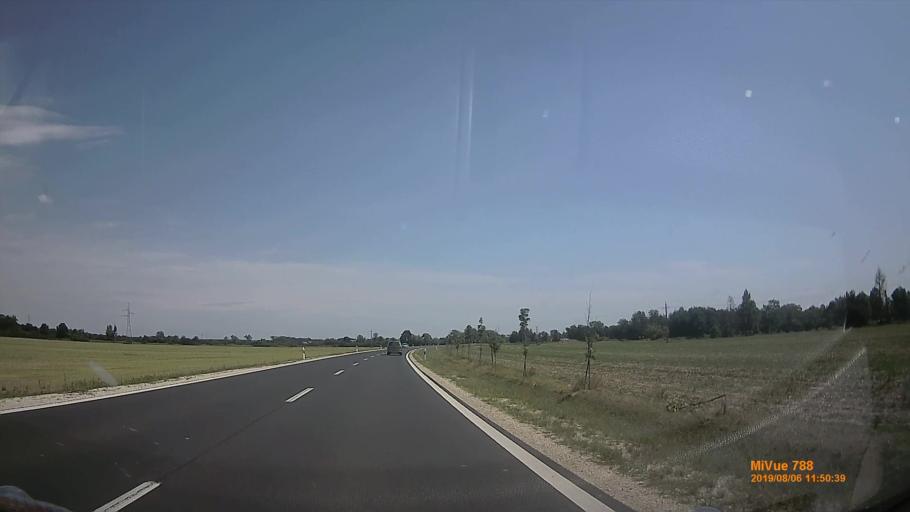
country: HU
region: Vas
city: Kormend
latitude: 47.0271
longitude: 16.6289
